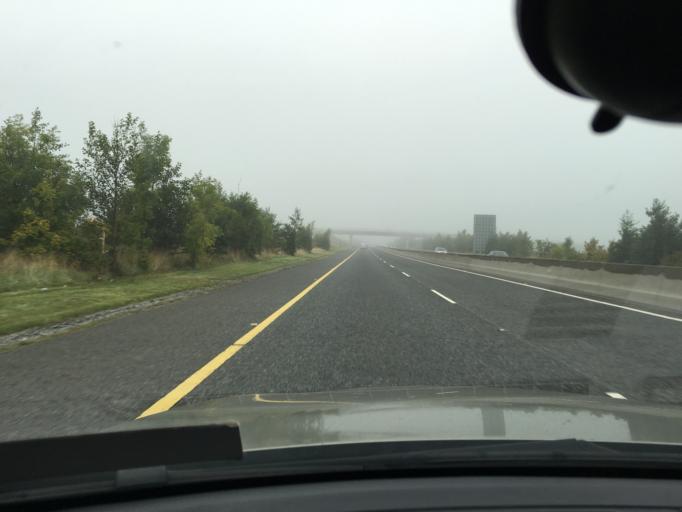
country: IE
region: Leinster
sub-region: An Iarmhi
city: Moate
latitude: 53.3856
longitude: -7.7061
